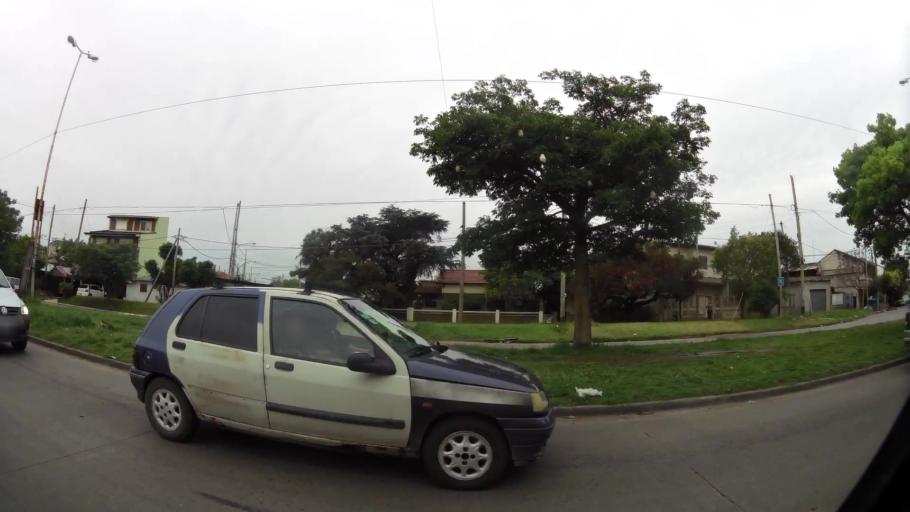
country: AR
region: Buenos Aires
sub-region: Partido de Lanus
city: Lanus
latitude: -34.7155
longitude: -58.3514
